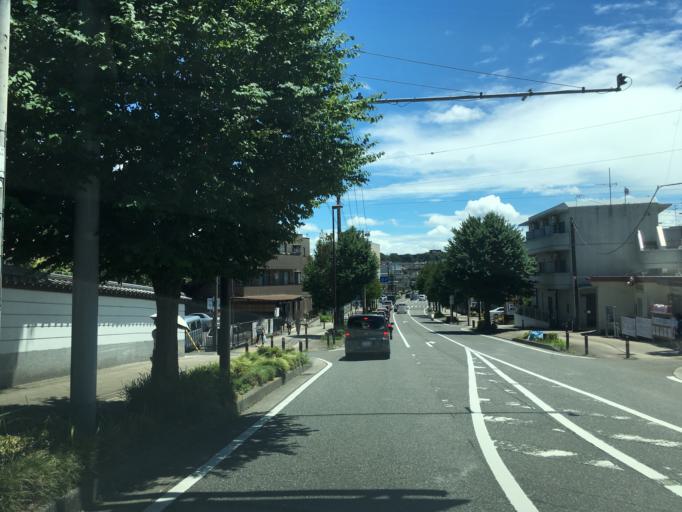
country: JP
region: Tokyo
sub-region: Machida-shi
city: Machida
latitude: 35.5288
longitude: 139.4969
